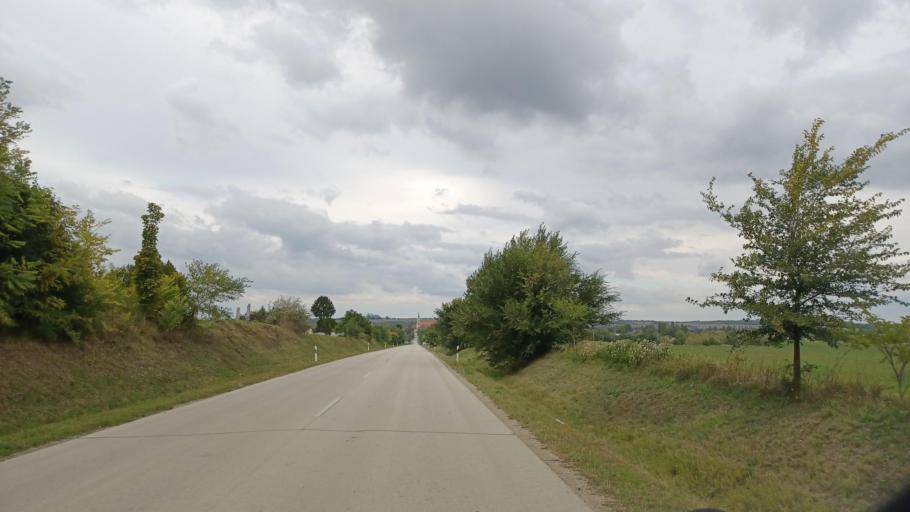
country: HU
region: Tolna
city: Simontornya
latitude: 46.7416
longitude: 18.5615
